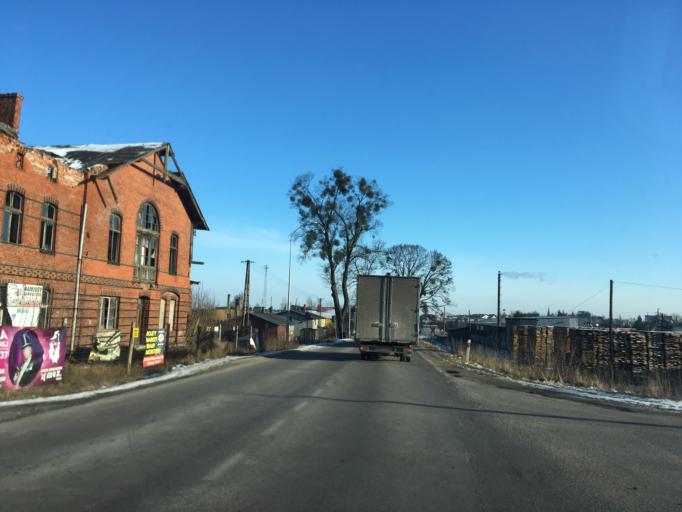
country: PL
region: Pomeranian Voivodeship
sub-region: Powiat starogardzki
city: Zblewo
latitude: 53.9455
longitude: 18.3116
